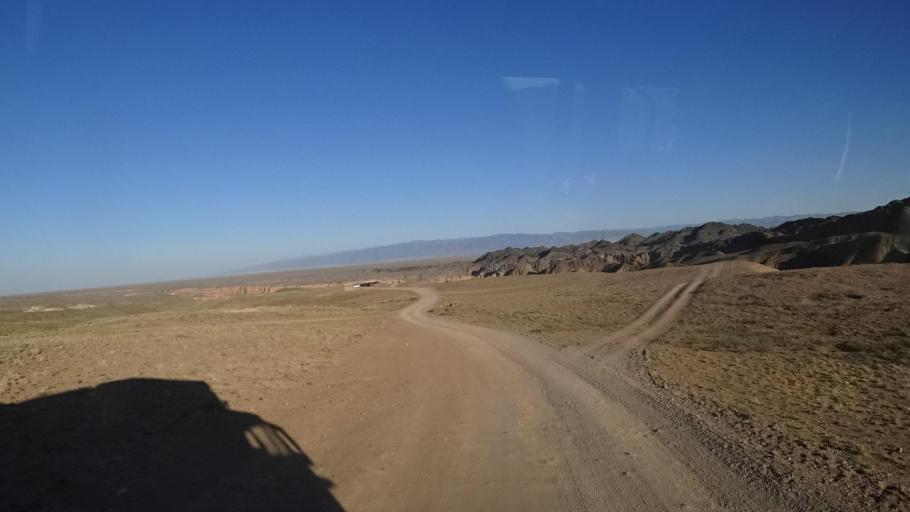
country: KZ
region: Almaty Oblysy
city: Kegen
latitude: 43.3556
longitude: 79.0572
